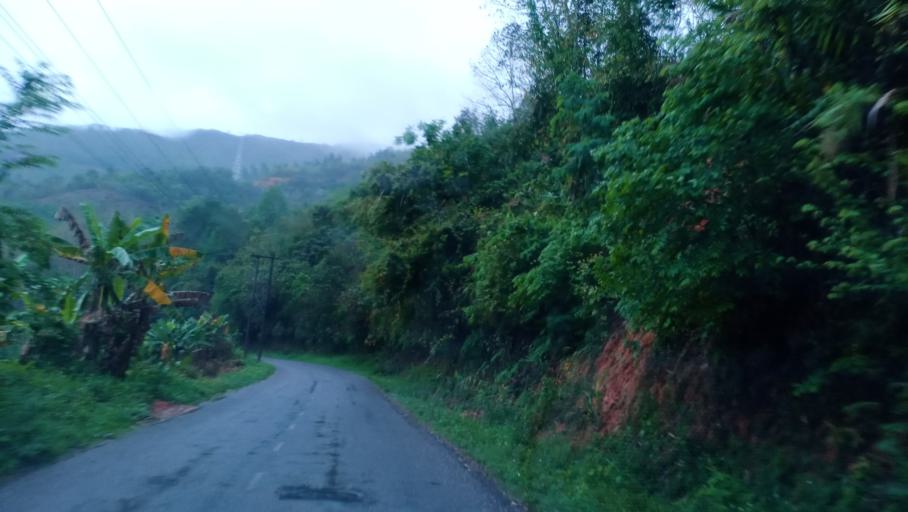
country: LA
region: Phongsali
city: Khoa
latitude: 21.0645
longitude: 102.4789
